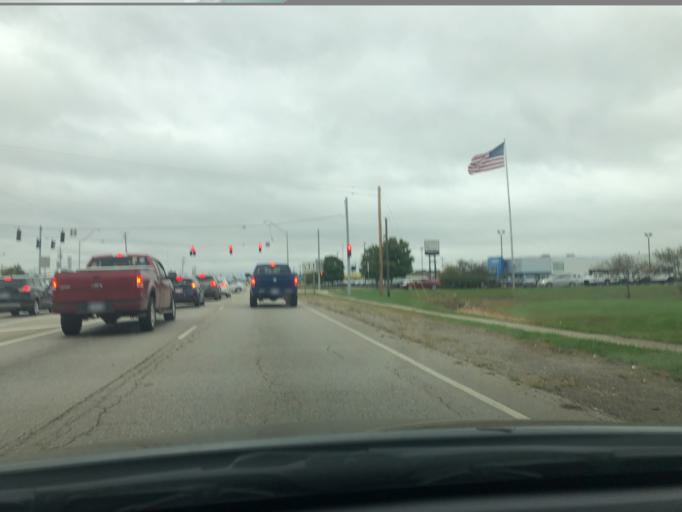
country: US
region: Ohio
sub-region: Union County
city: Marysville
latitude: 40.2389
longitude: -83.3453
